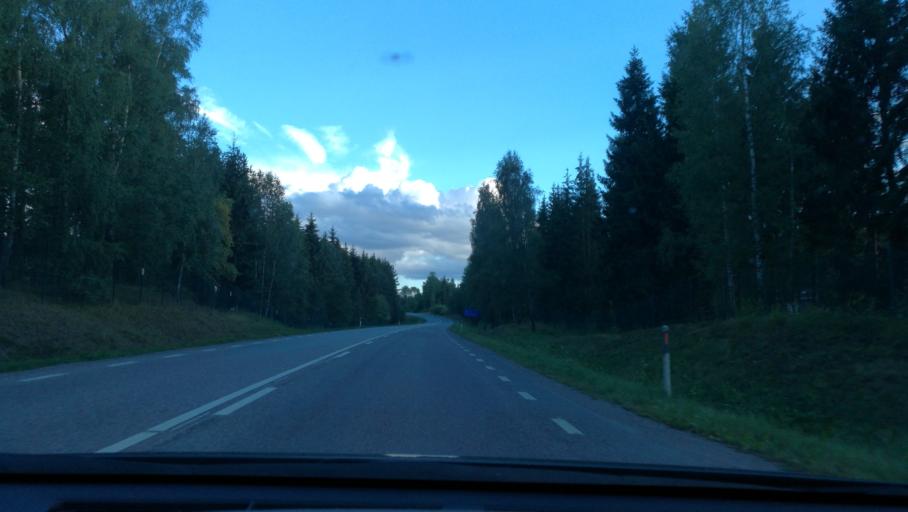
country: SE
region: Soedermanland
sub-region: Katrineholms Kommun
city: Katrineholm
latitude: 59.0129
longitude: 16.2135
